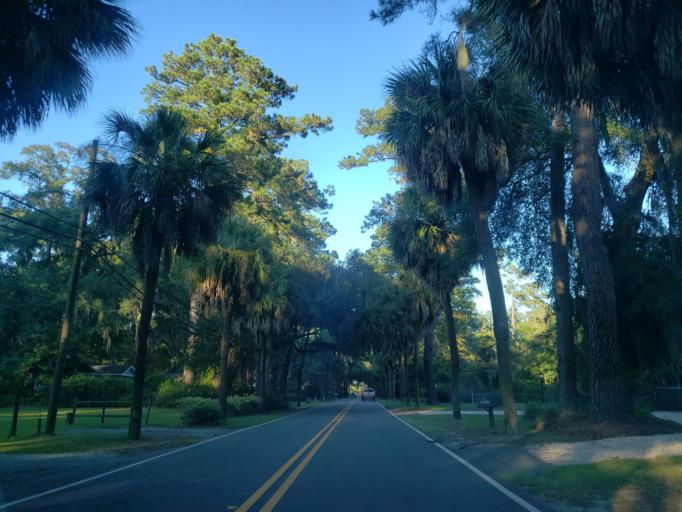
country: US
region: Georgia
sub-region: Chatham County
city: Isle of Hope
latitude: 31.9956
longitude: -81.0631
